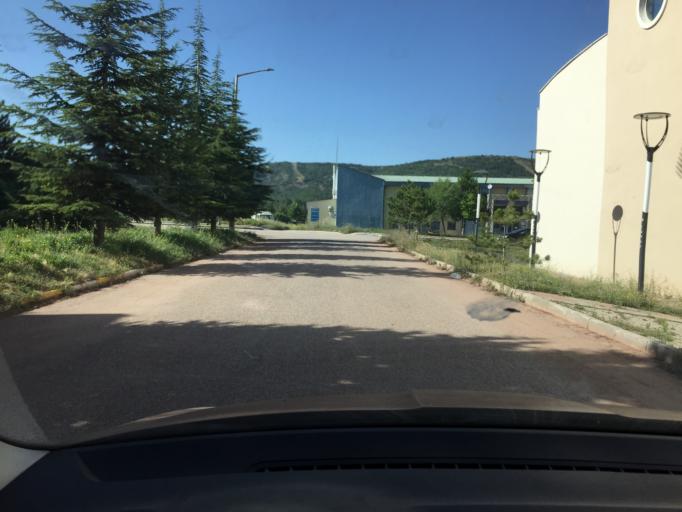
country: TR
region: Eskisehir
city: Eskisehir
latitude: 39.7475
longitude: 30.4749
